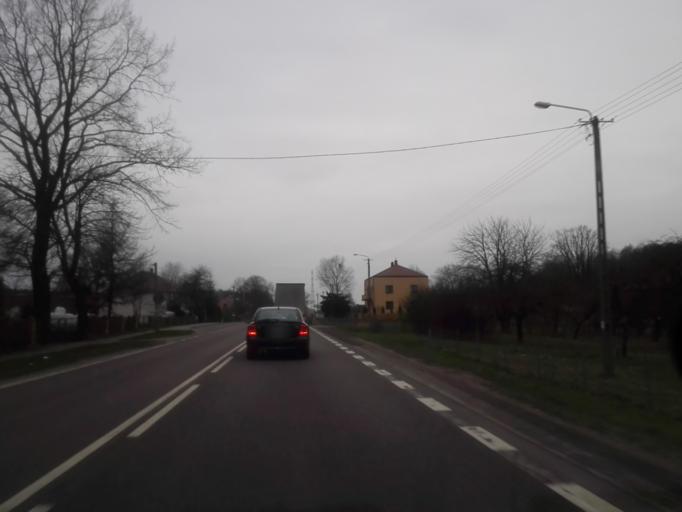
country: PL
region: Podlasie
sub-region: Powiat grajewski
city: Szczuczyn
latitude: 53.5939
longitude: 22.3458
